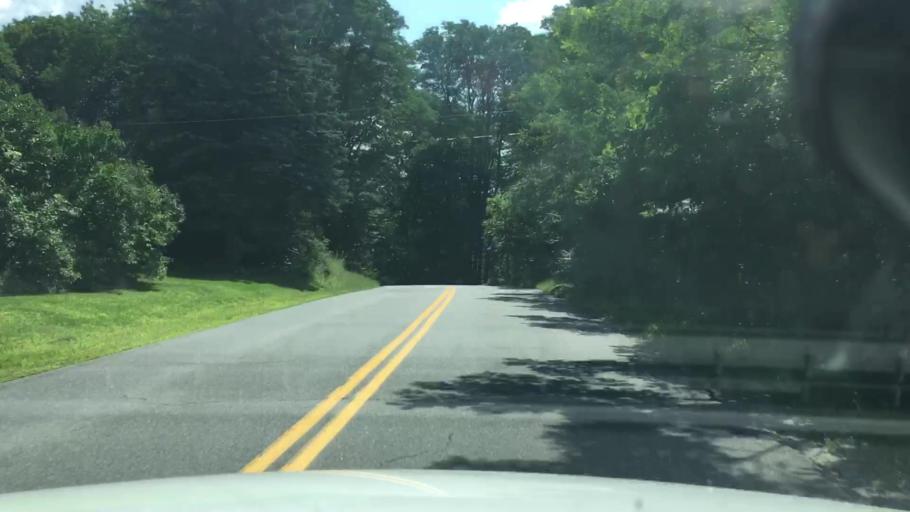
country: US
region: Maine
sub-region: Somerset County
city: Skowhegan
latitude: 44.7249
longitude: -69.7047
